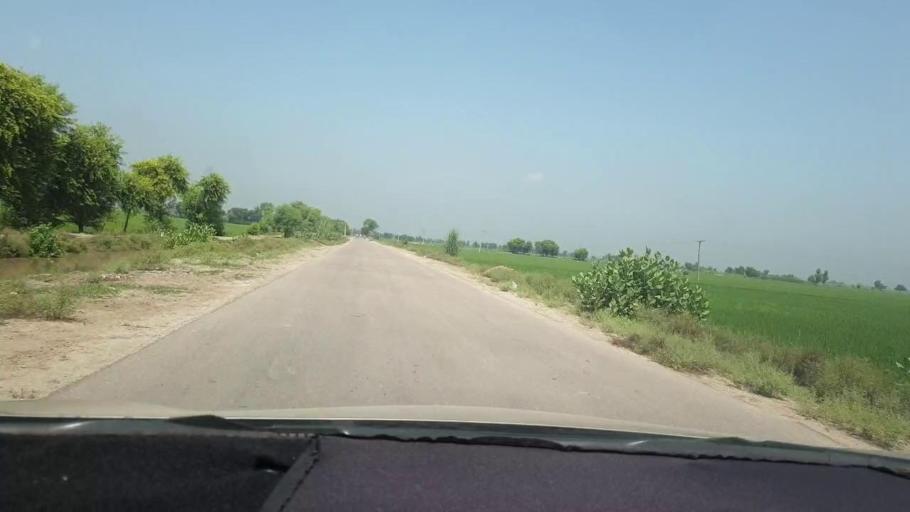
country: PK
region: Sindh
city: Miro Khan
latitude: 27.7628
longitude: 68.0756
